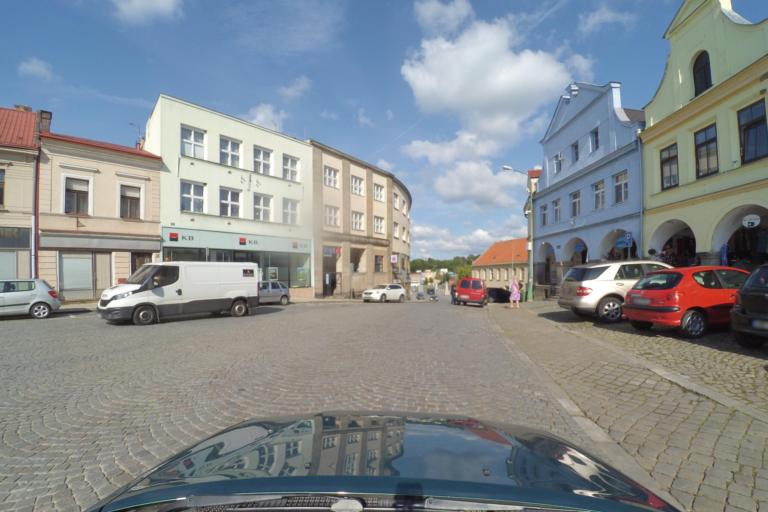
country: CZ
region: Kralovehradecky
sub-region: Okres Nachod
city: Jaromer
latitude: 50.3556
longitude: 15.9178
